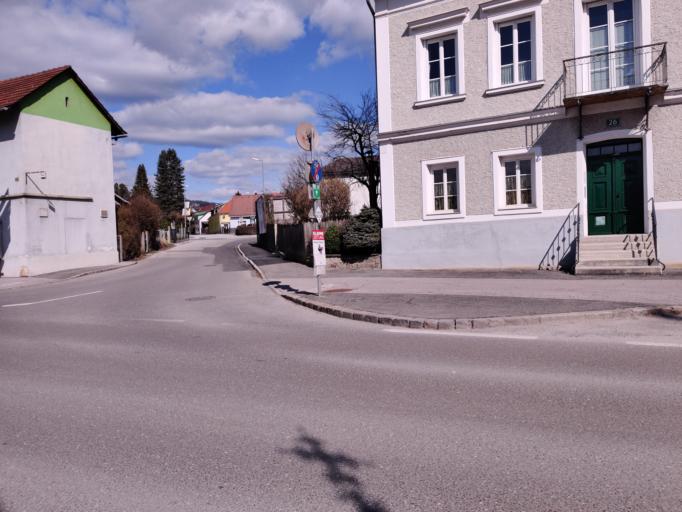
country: AT
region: Styria
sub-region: Politischer Bezirk Voitsberg
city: Voitsberg
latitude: 47.0518
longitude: 15.1430
